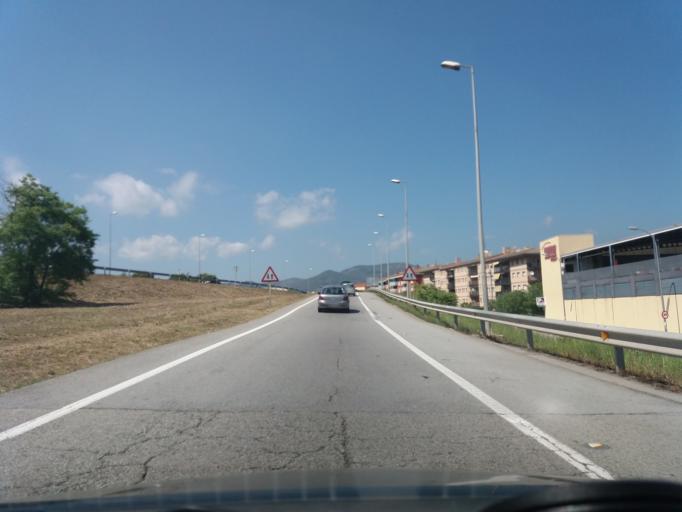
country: ES
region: Catalonia
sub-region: Provincia de Barcelona
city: Abrera
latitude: 41.5173
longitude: 1.8982
